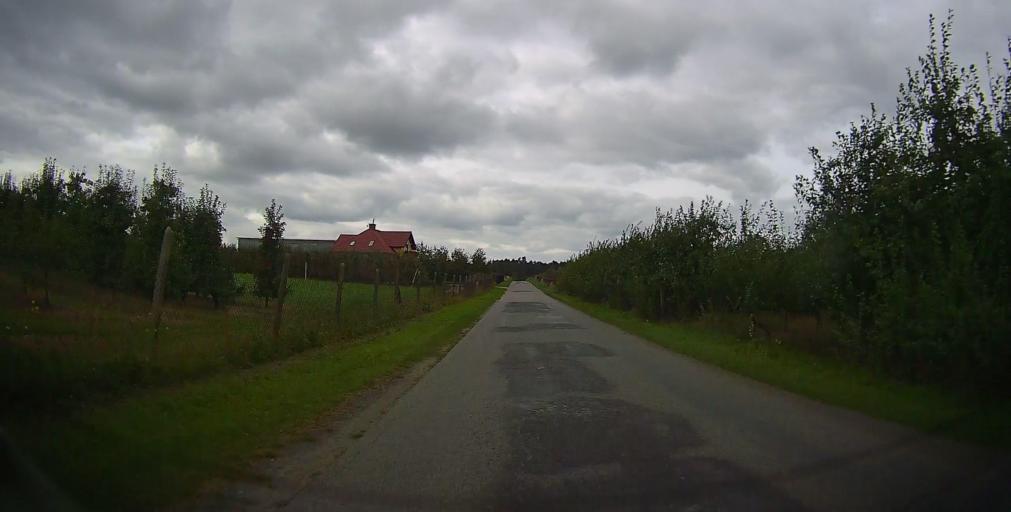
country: PL
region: Masovian Voivodeship
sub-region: Powiat grojecki
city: Goszczyn
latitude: 51.7702
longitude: 20.8663
